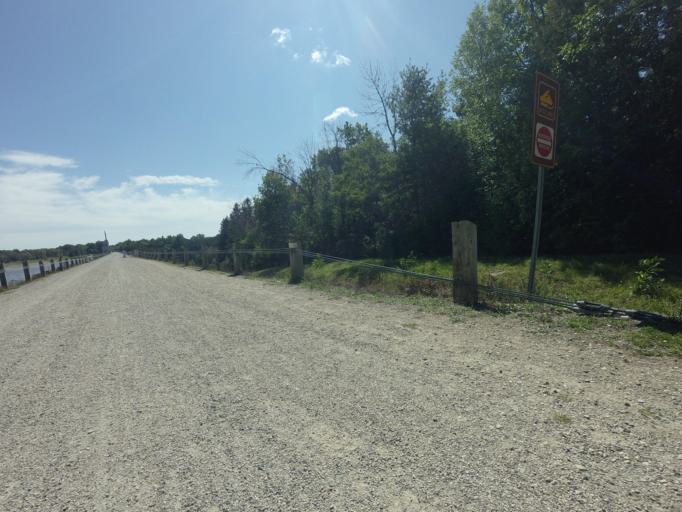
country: CA
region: Ontario
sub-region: Wellington County
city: Guelph
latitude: 43.7354
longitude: -80.3410
